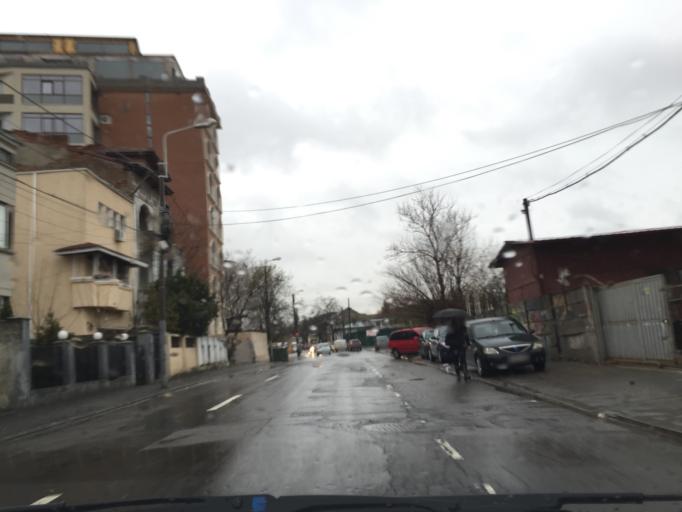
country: RO
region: Bucuresti
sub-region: Municipiul Bucuresti
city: Bucuresti
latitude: 44.4214
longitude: 26.0845
